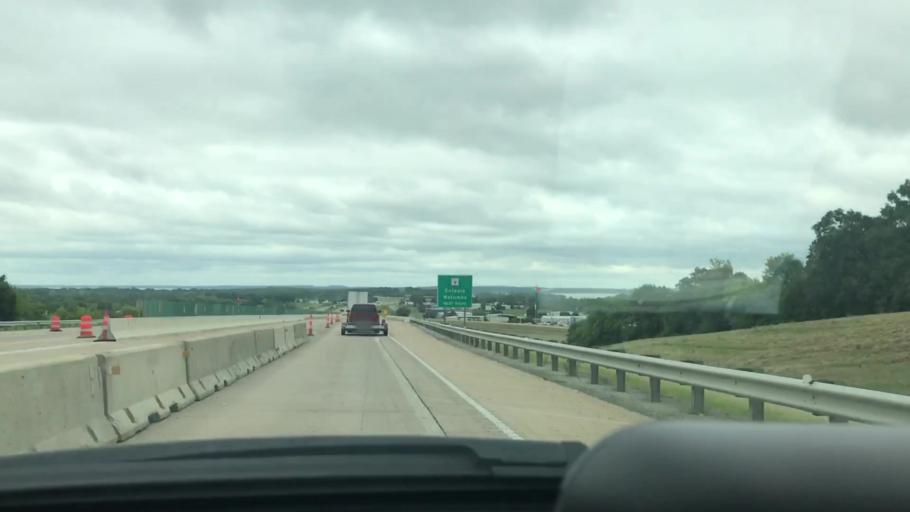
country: US
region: Oklahoma
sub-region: McIntosh County
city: Eufaula
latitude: 35.2911
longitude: -95.5931
